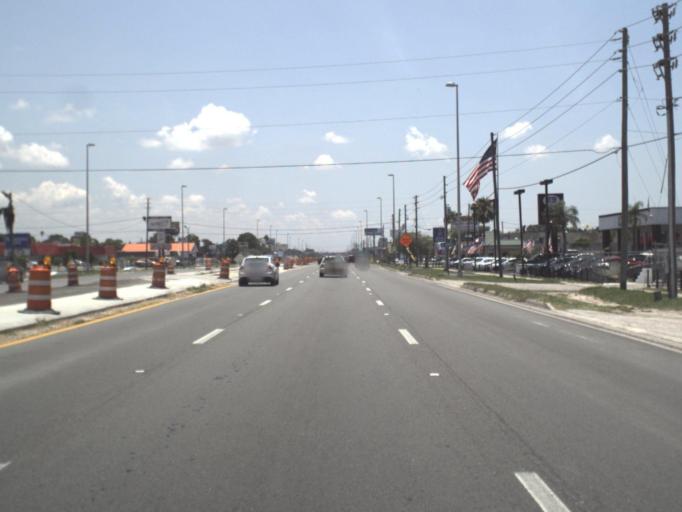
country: US
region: Florida
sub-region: Pasco County
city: Port Richey
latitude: 28.2585
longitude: -82.7279
